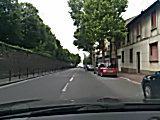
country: FR
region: Ile-de-France
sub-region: Departement des Hauts-de-Seine
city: Montrouge
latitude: 48.8100
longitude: 2.3161
